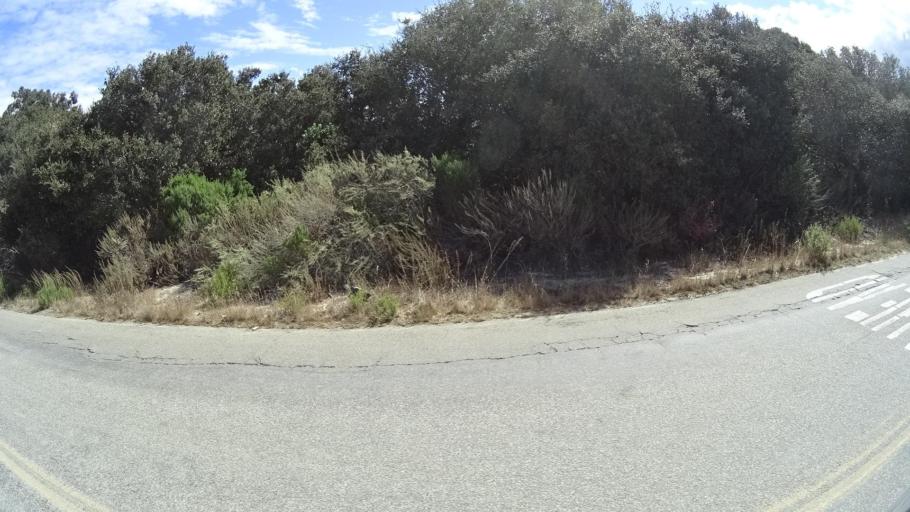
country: US
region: California
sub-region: Monterey County
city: Salinas
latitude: 36.5965
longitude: -121.6262
